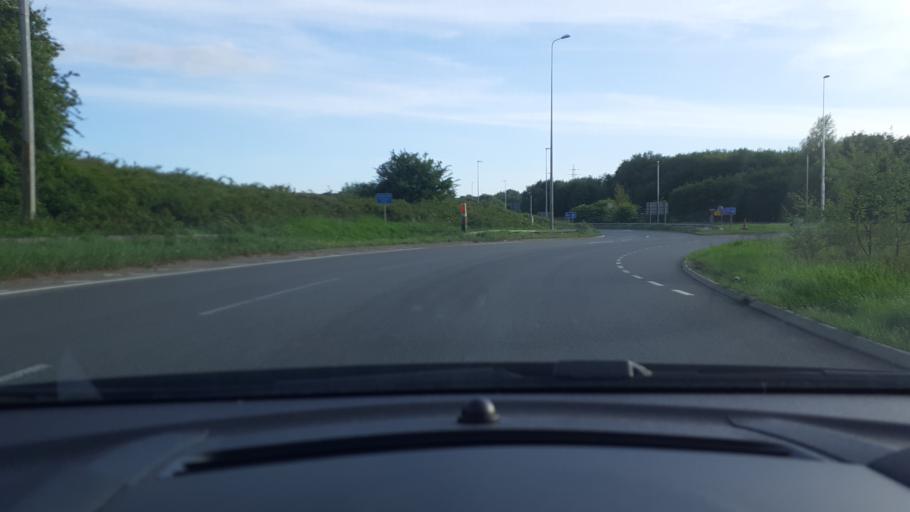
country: GB
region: England
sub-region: Borough of Wigan
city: Shevington
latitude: 53.5342
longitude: -2.6945
